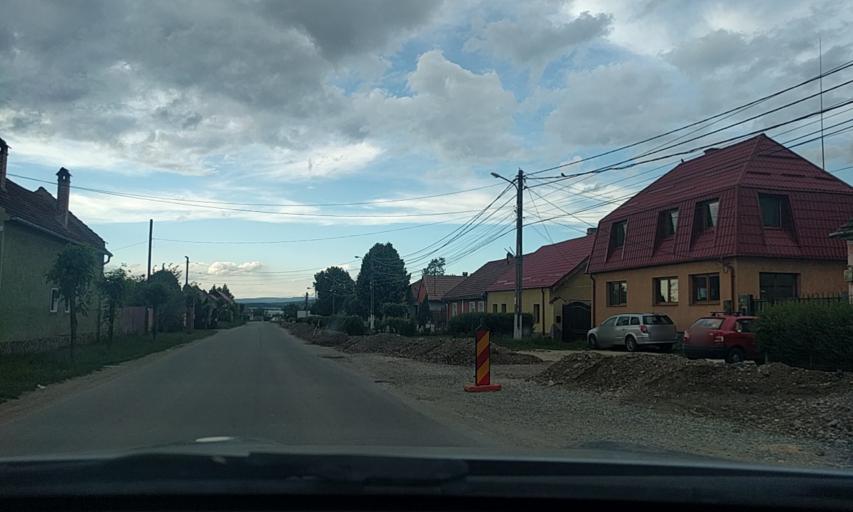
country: RO
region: Brasov
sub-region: Comuna Harman
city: Harman
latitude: 45.7156
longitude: 25.6947
